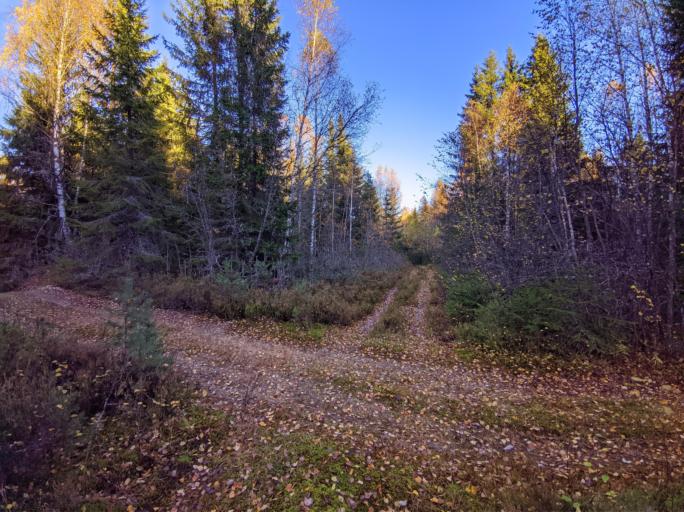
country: NO
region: Akershus
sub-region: Eidsvoll
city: Raholt
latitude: 60.2326
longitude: 11.1137
